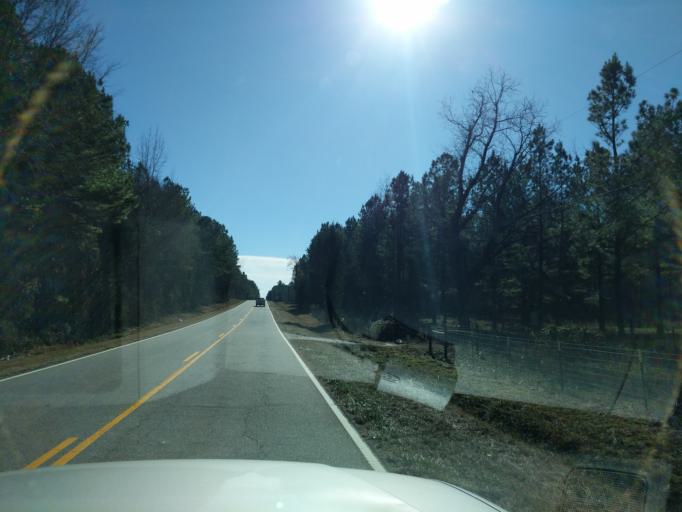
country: US
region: South Carolina
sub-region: Saluda County
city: Saluda
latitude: 34.1236
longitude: -81.8383
